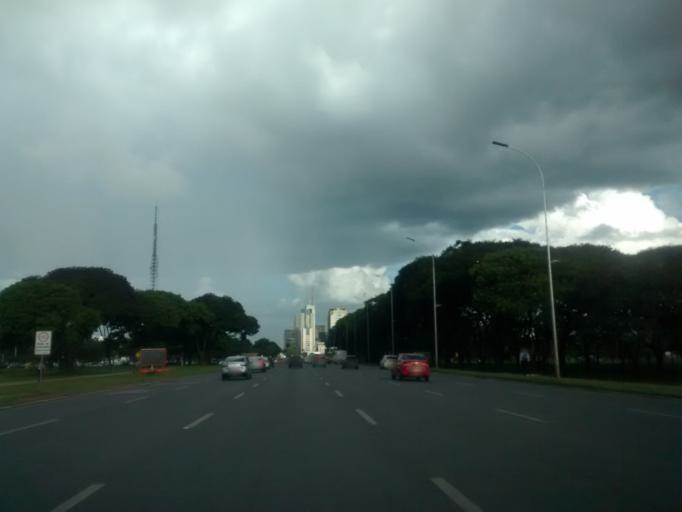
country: BR
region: Federal District
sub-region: Brasilia
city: Brasilia
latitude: -15.7898
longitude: -47.9017
